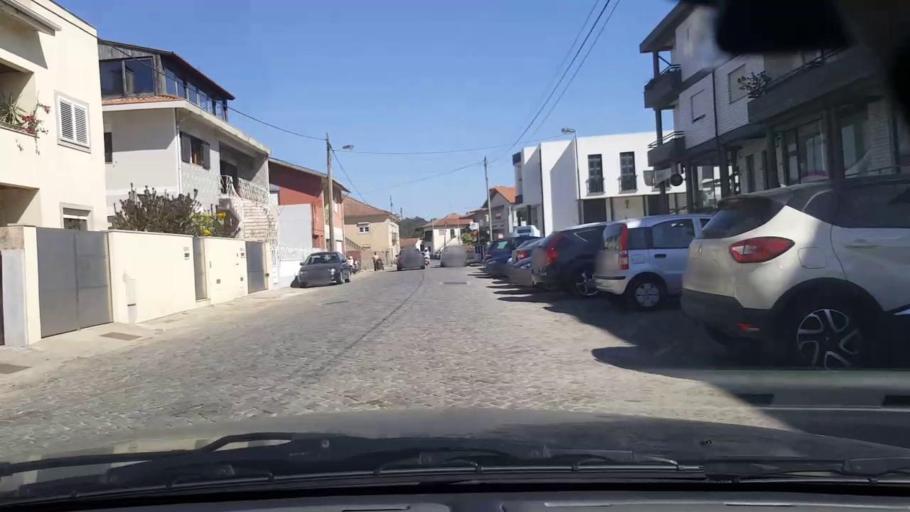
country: PT
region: Porto
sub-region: Matosinhos
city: Lavra
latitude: 41.2941
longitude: -8.7233
